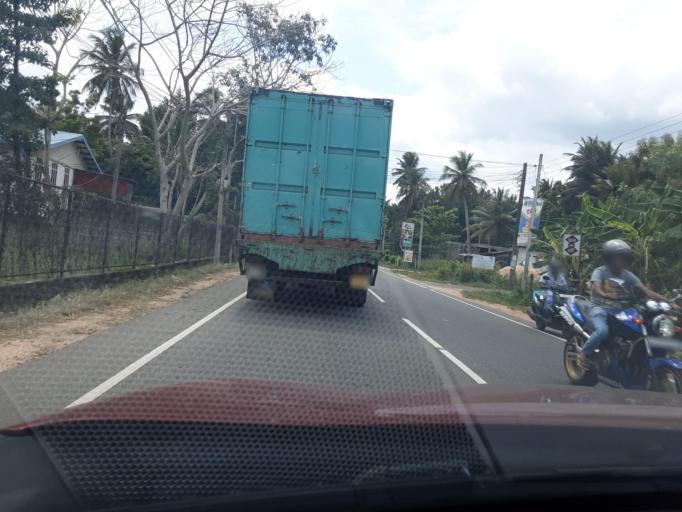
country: LK
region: North Western
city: Kuliyapitiya
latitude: 7.4479
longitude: 80.2004
